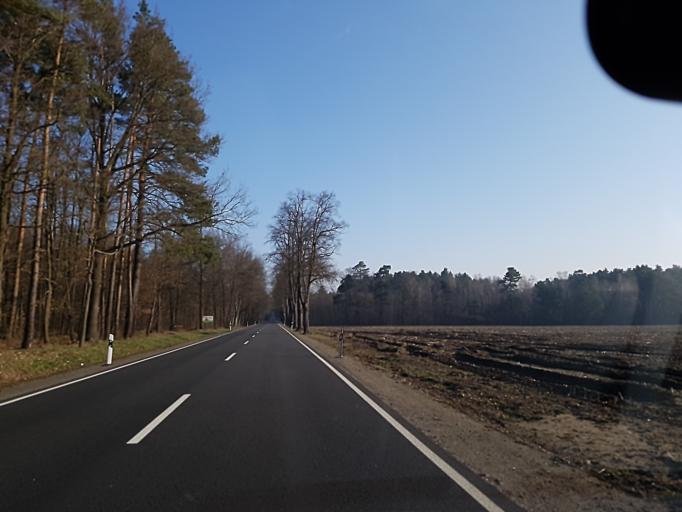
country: DE
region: Brandenburg
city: Bronkow
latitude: 51.6869
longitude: 13.9161
